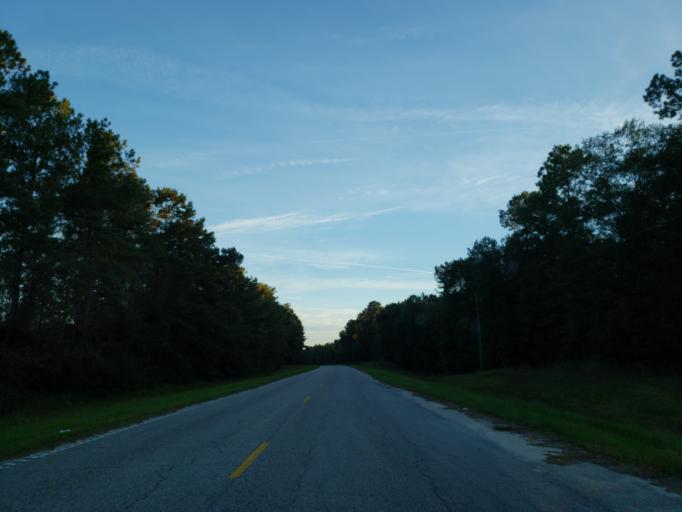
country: US
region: Mississippi
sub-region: Wayne County
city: Belmont
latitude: 31.4153
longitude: -88.4711
